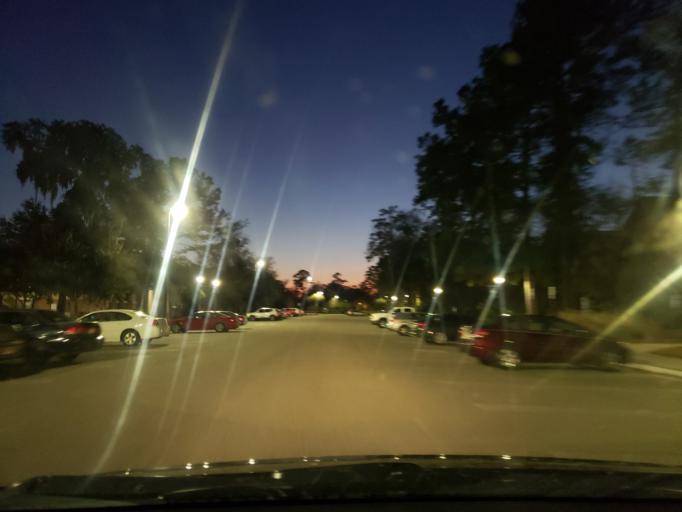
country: US
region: Georgia
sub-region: Chatham County
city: Montgomery
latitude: 31.9779
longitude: -81.1644
